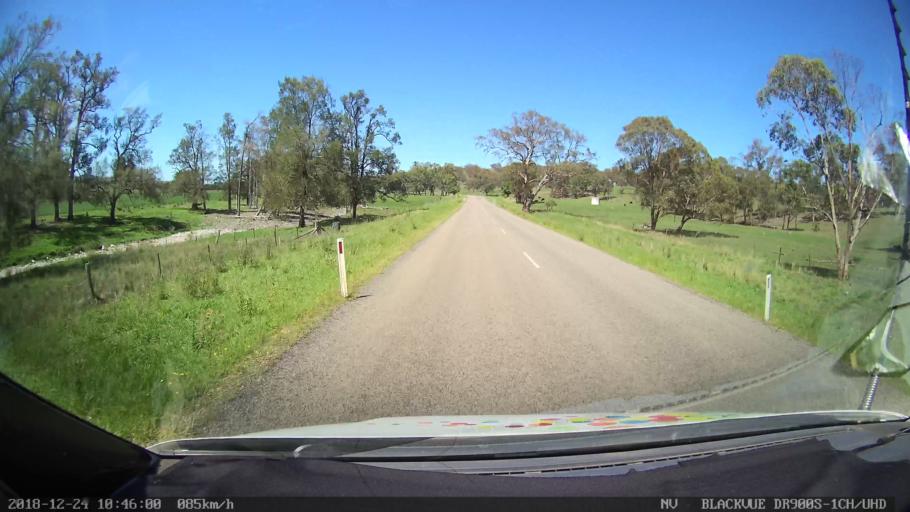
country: AU
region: New South Wales
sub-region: Upper Hunter Shire
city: Merriwa
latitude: -31.9082
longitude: 150.4316
